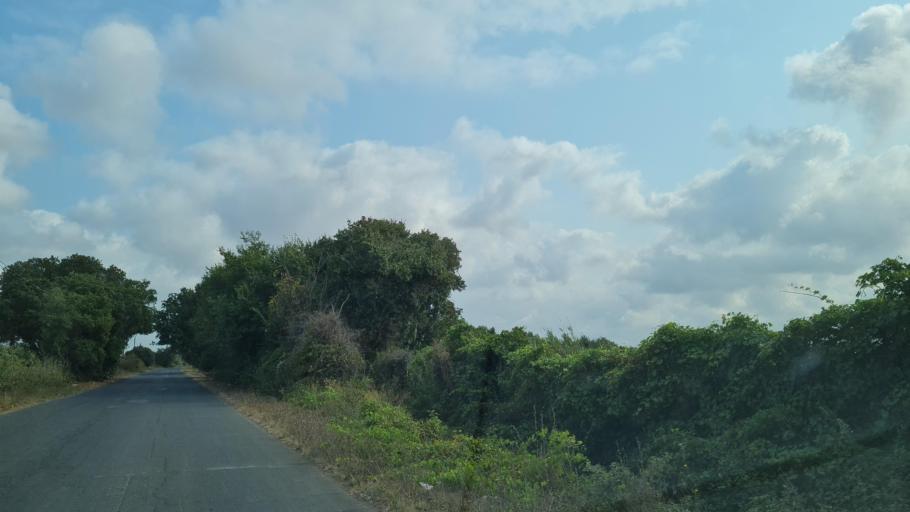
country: IT
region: Latium
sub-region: Provincia di Viterbo
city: Montalto di Castro
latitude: 42.3168
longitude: 11.6095
